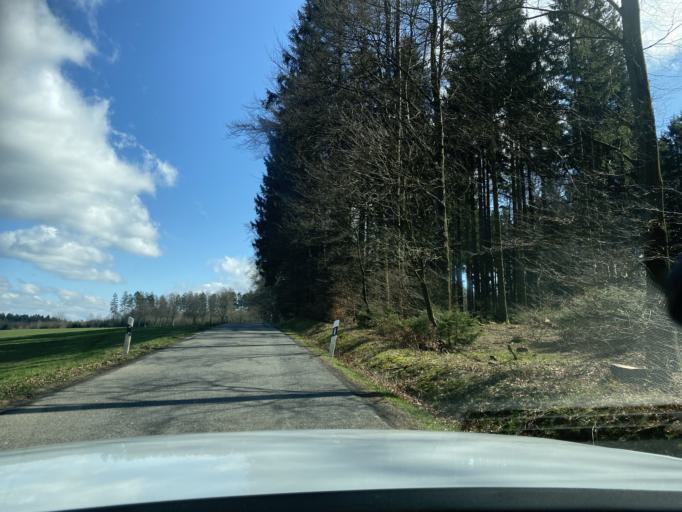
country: DE
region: North Rhine-Westphalia
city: Wipperfurth
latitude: 51.1501
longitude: 7.4031
